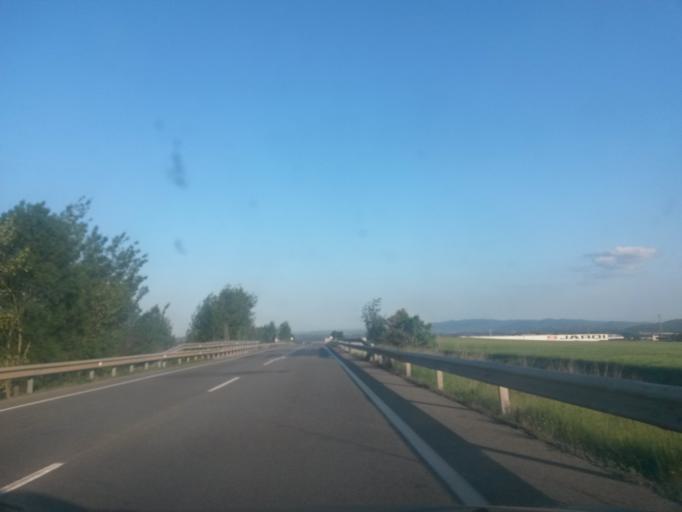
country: ES
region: Catalonia
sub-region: Provincia de Girona
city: Banyoles
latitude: 42.1270
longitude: 2.7790
